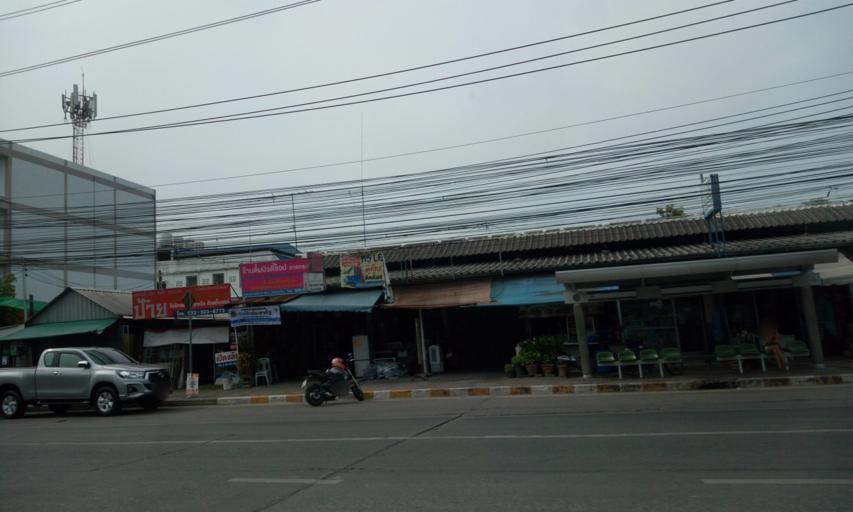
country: TH
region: Bangkok
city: Lat Krabang
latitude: 13.7221
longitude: 100.7535
